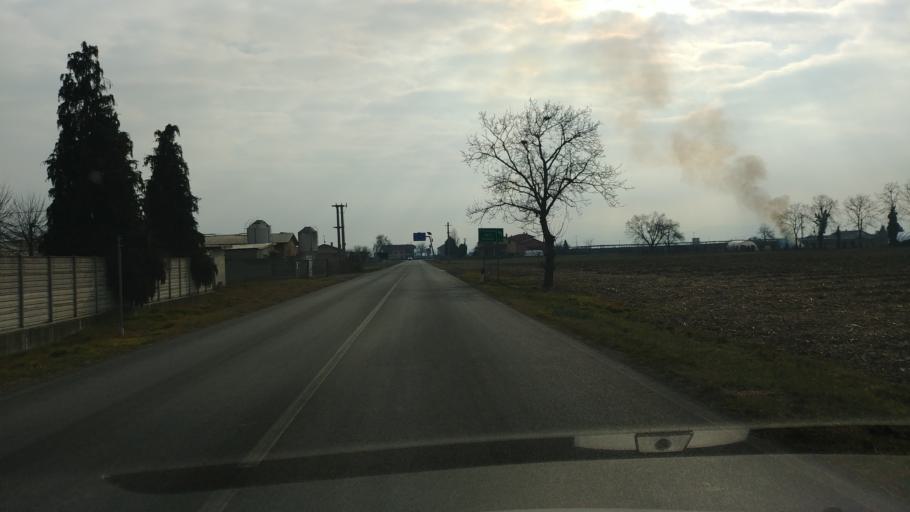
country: IT
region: Piedmont
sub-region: Provincia di Cuneo
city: Castelletto Stura
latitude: 44.4490
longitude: 7.6479
